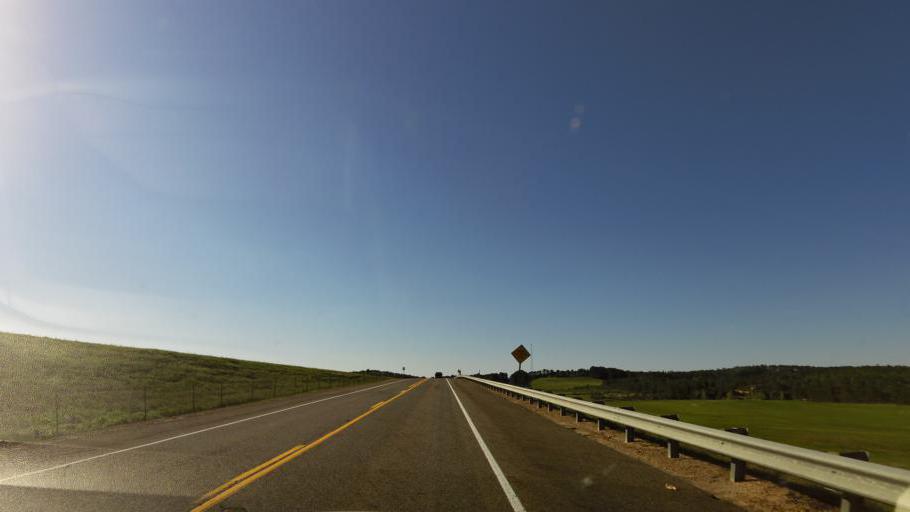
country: US
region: Louisiana
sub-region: Vernon Parish
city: New Llano
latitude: 31.1931
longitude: -93.5708
